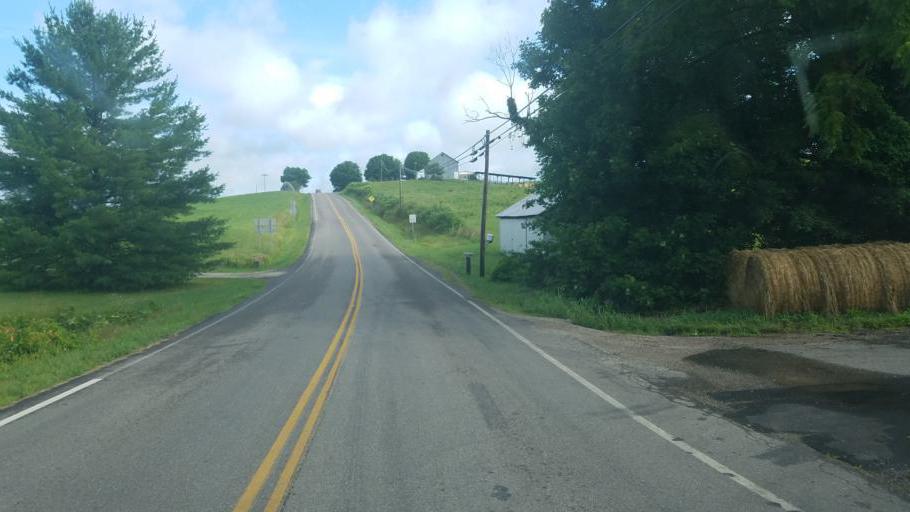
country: US
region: Ohio
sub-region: Gallia County
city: Gallipolis
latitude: 38.7964
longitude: -82.3977
